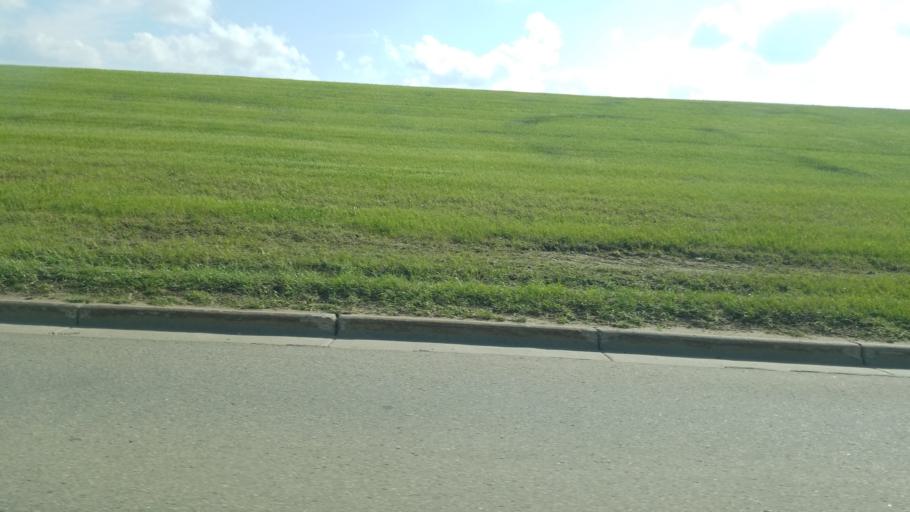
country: CA
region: Saskatchewan
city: Lloydminster
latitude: 53.2727
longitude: -110.0317
